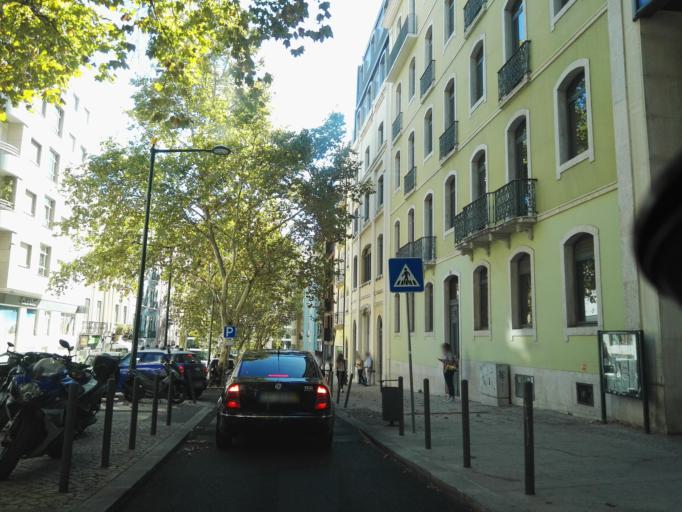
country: PT
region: Lisbon
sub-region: Lisbon
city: Lisbon
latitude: 38.7305
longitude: -9.1482
